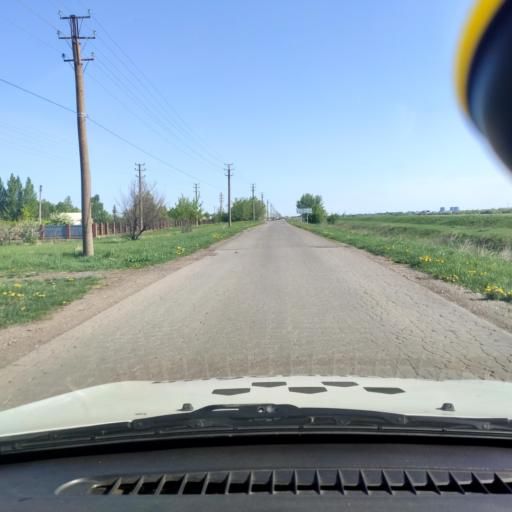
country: RU
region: Samara
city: Podstepki
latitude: 53.5342
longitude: 49.1991
